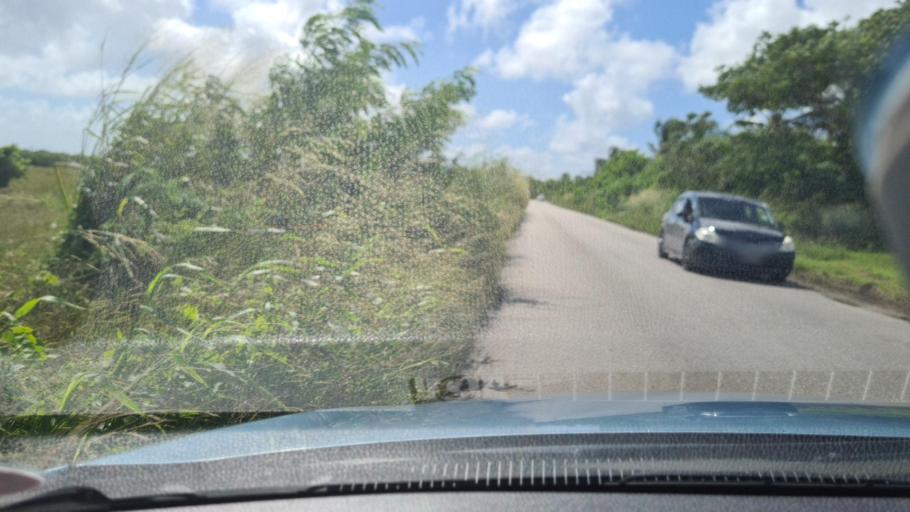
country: BB
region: Christ Church
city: Oistins
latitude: 13.0927
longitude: -59.5204
